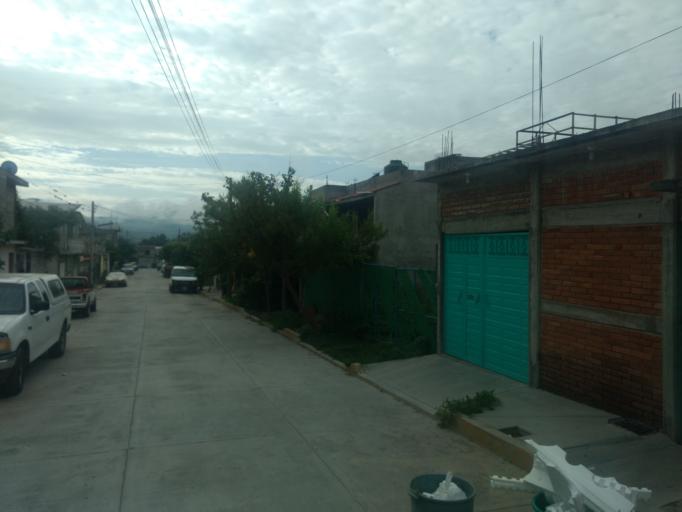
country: MX
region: Oaxaca
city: Ciudad de Huajuapam de Leon
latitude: 17.8053
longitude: -97.7911
